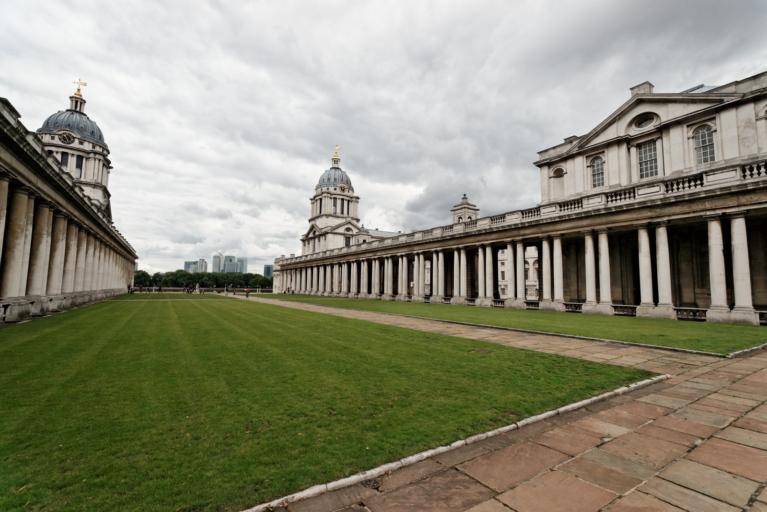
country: GB
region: England
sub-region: Greater London
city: Blackheath
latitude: 51.4824
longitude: -0.0050
